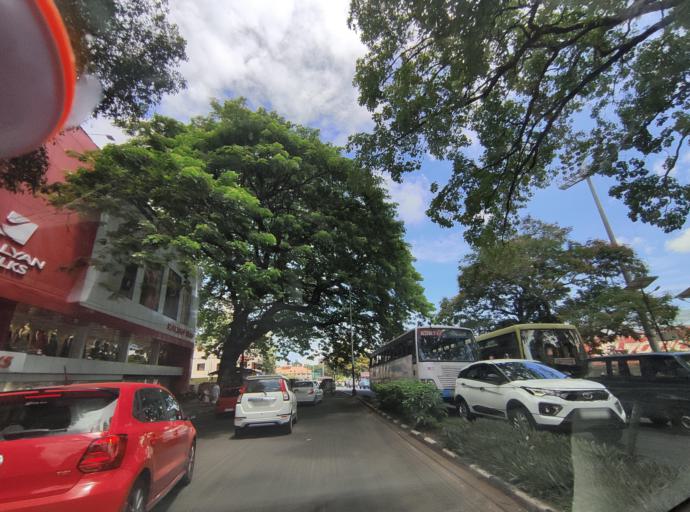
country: IN
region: Kerala
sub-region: Thiruvananthapuram
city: Thiruvananthapuram
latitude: 8.5053
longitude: 76.9516
